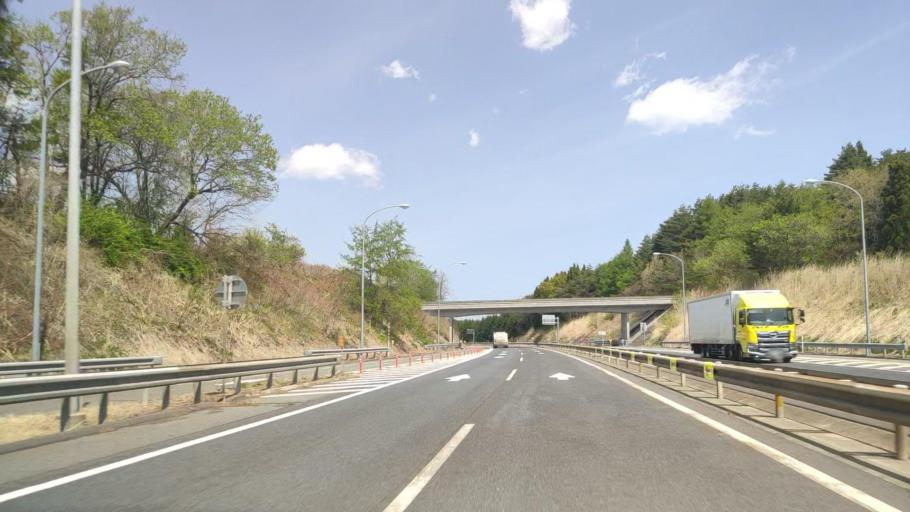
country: JP
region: Aomori
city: Hachinohe
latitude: 40.4088
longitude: 141.4438
